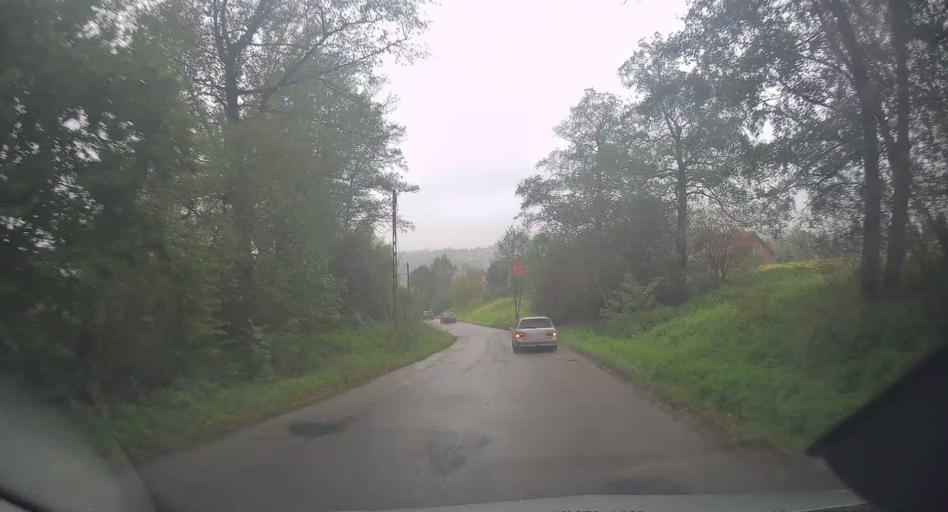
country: PL
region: Lesser Poland Voivodeship
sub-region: Powiat krakowski
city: Ochojno
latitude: 49.9699
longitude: 19.9980
